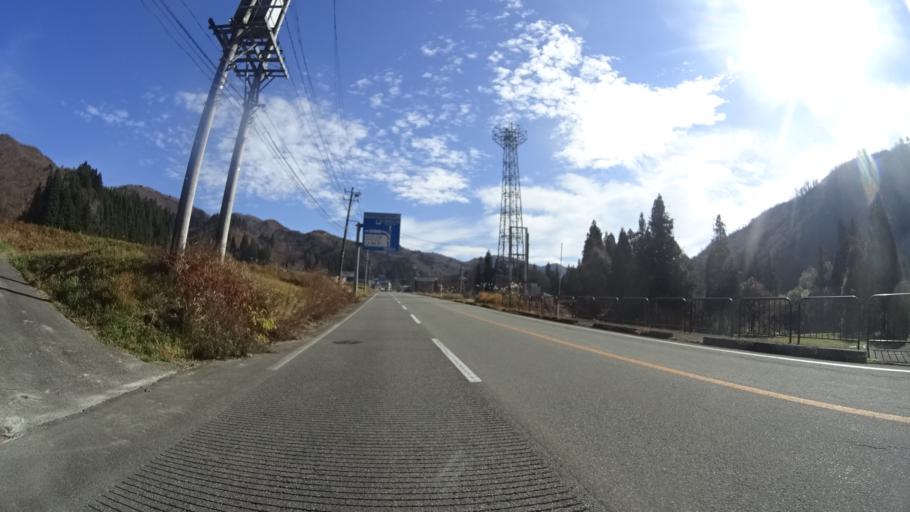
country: JP
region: Niigata
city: Muikamachi
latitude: 37.2057
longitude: 139.0686
